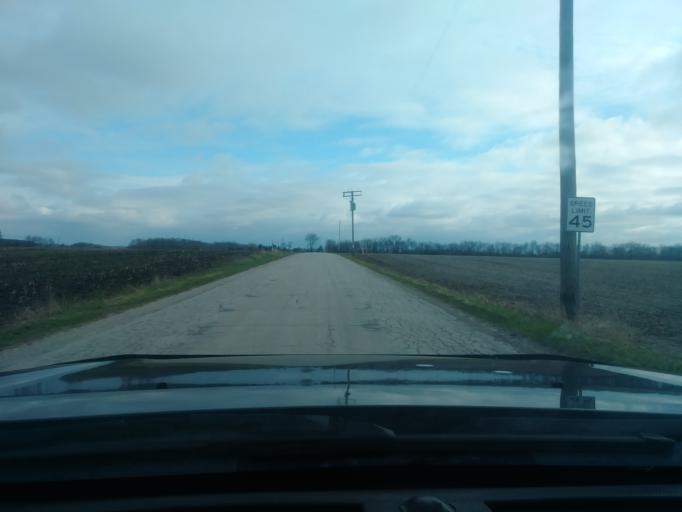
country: US
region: Indiana
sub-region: LaPorte County
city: LaPorte
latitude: 41.5664
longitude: -86.7983
